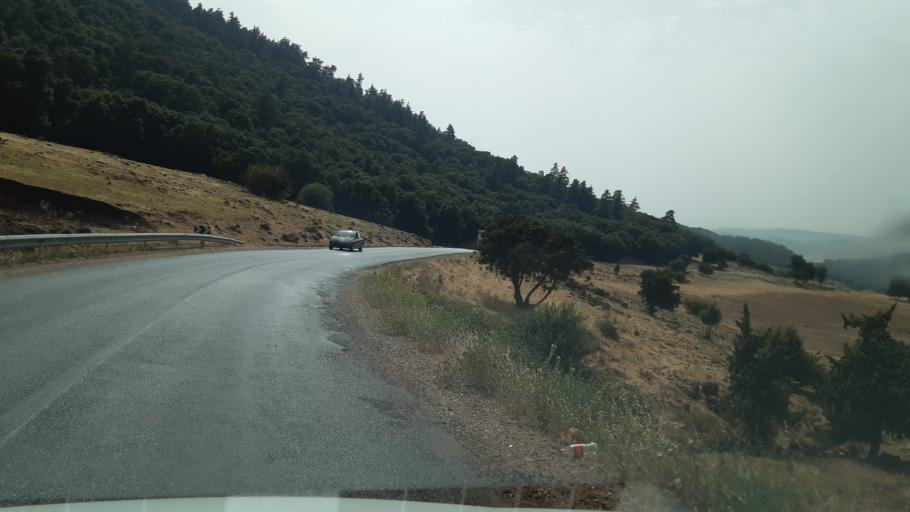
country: MA
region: Meknes-Tafilalet
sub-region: Ifrane
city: Azrou
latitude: 33.4255
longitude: -5.1946
